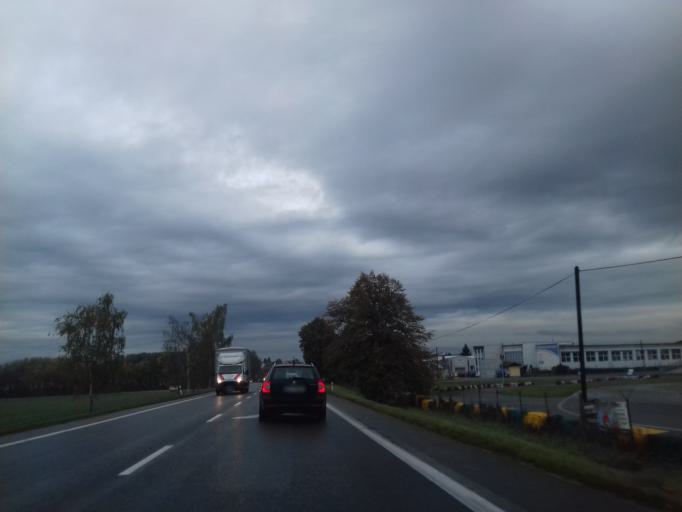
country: CZ
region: Pardubicky
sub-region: Okres Pardubice
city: Vysoke Myto
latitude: 49.9391
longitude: 16.1685
